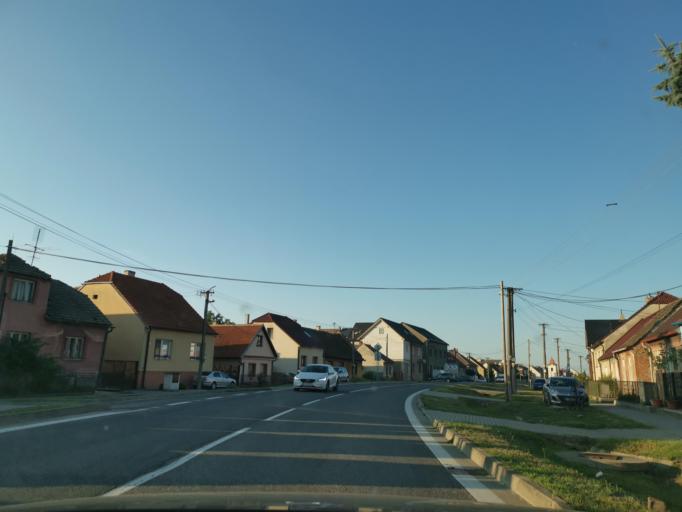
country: CZ
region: South Moravian
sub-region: Okres Breclav
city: Lanzhot
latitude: 48.6535
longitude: 17.0137
